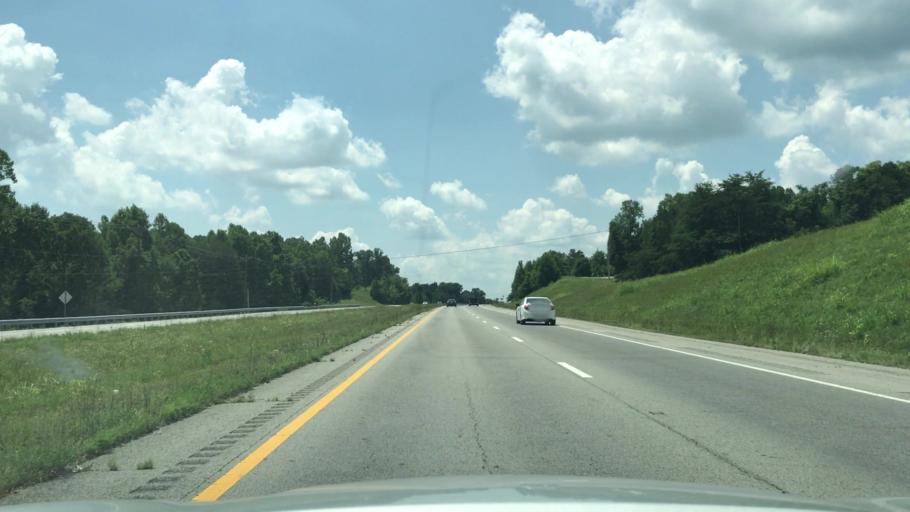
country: US
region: Tennessee
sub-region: Overton County
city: Livingston
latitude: 36.3460
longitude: -85.3467
